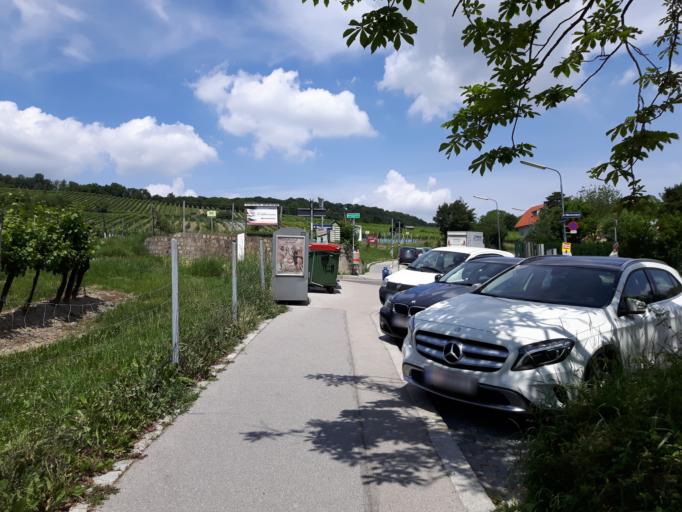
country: AT
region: Lower Austria
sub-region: Politischer Bezirk Wien-Umgebung
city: Klosterneuburg
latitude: 48.2524
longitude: 16.3079
